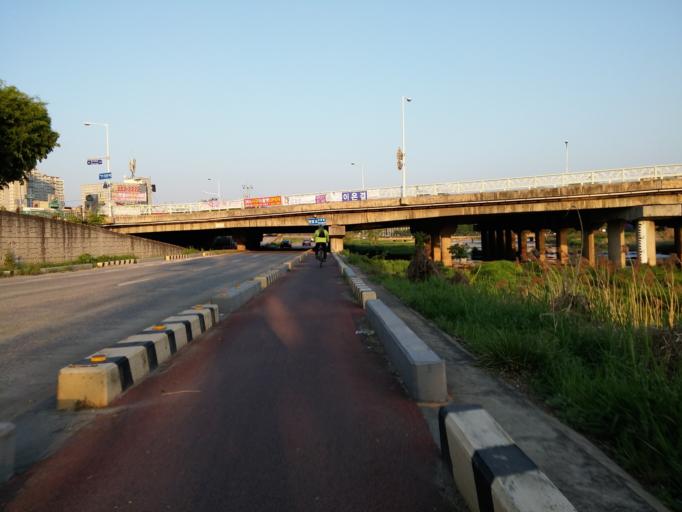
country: KR
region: Daejeon
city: Daejeon
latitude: 36.3391
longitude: 127.4180
